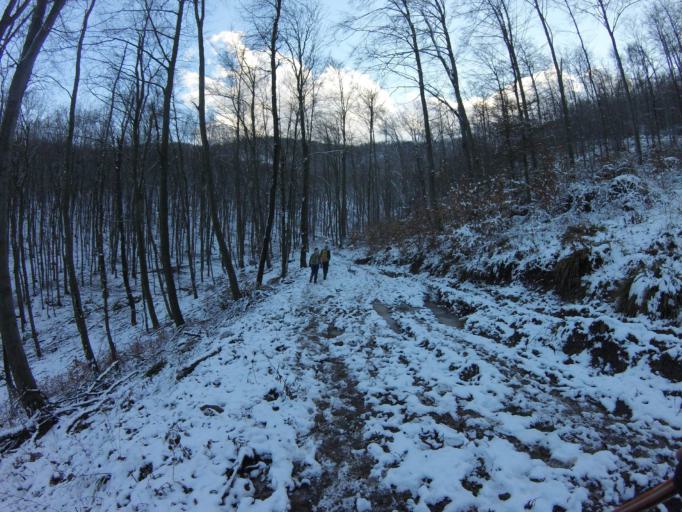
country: HU
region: Pest
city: Pilisszentkereszt
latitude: 47.7257
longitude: 18.8967
